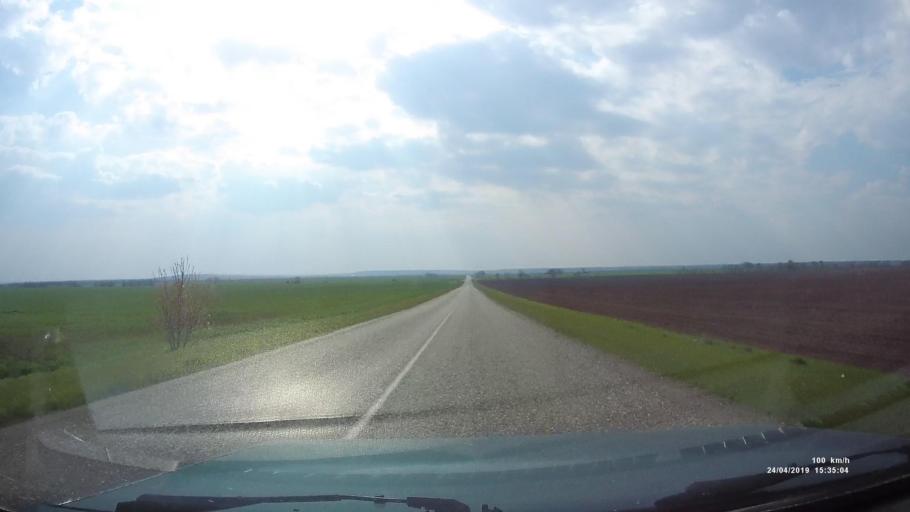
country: RU
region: Kalmykiya
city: Yashalta
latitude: 46.5994
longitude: 42.9017
